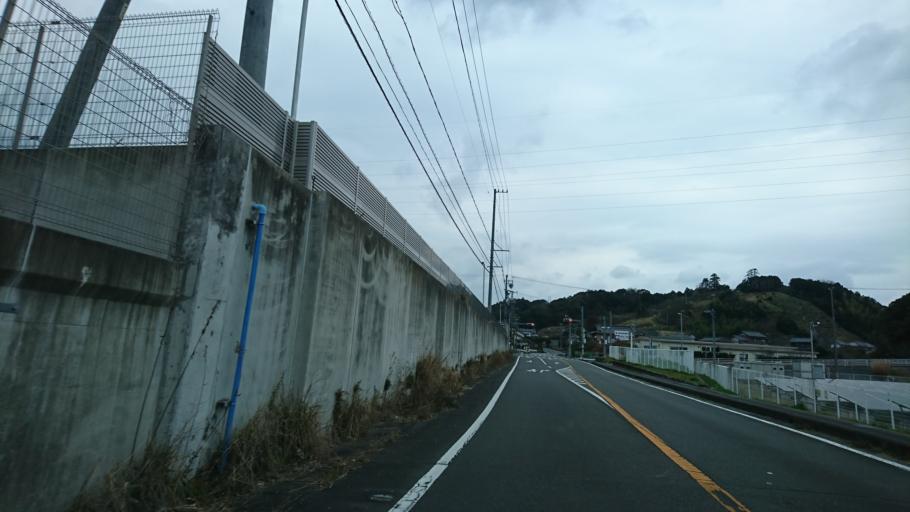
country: JP
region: Shizuoka
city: Sagara
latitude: 34.7287
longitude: 138.1812
